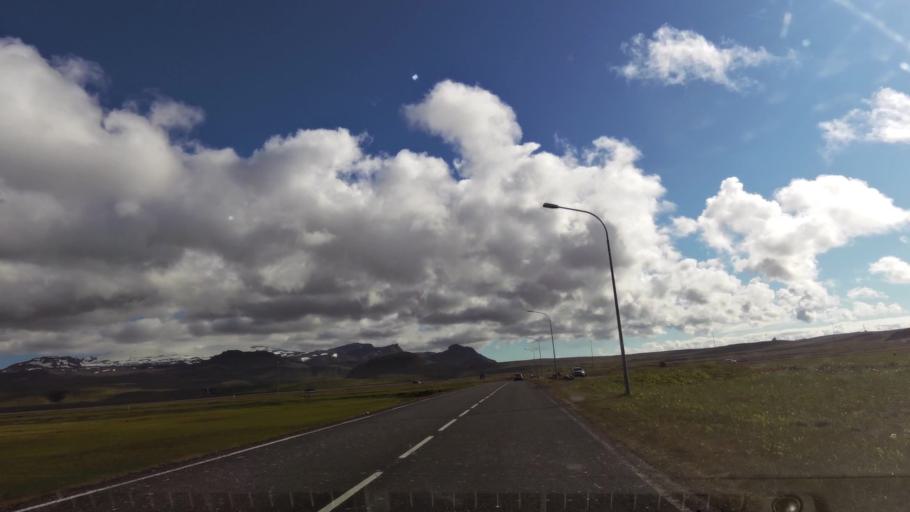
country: IS
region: West
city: Olafsvik
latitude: 64.9207
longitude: -23.8188
